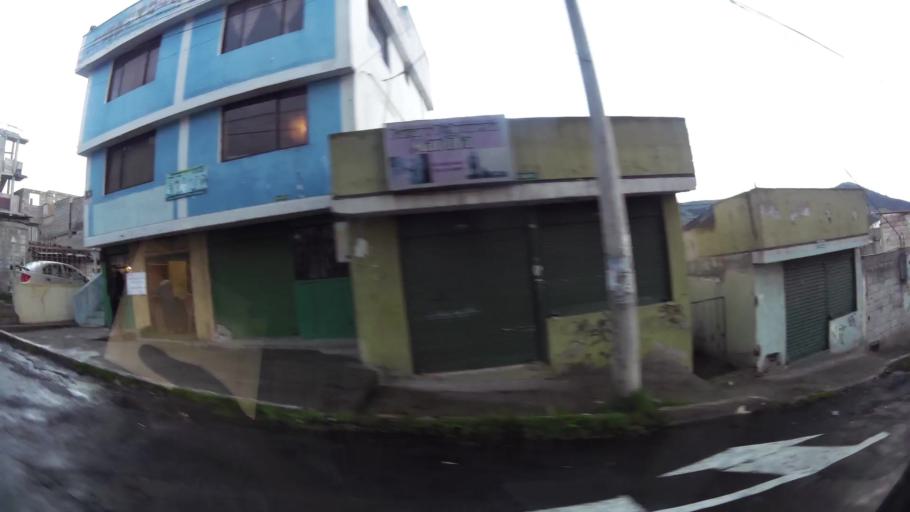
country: EC
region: Pichincha
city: Quito
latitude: -0.0891
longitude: -78.5138
